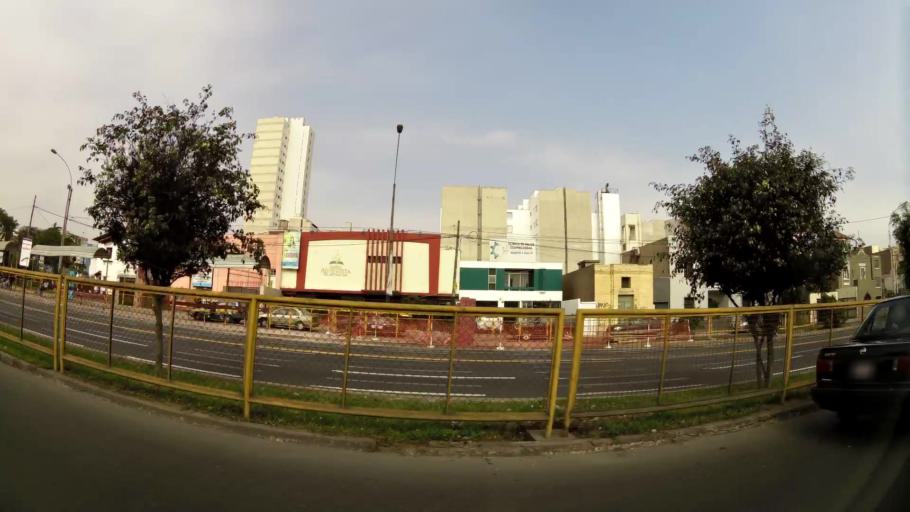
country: PE
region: Lima
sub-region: Lima
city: San Isidro
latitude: -12.0812
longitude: -77.0589
